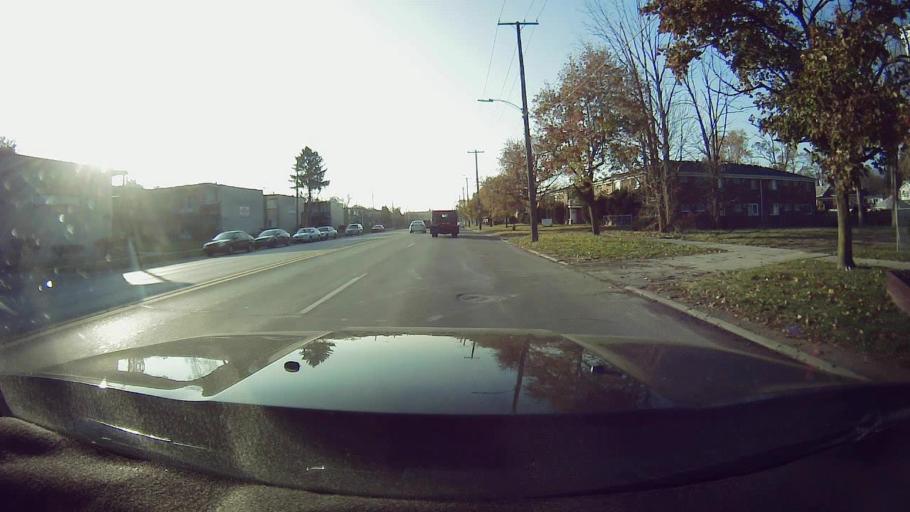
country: US
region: Michigan
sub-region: Oakland County
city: Oak Park
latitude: 42.4005
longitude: -83.1987
